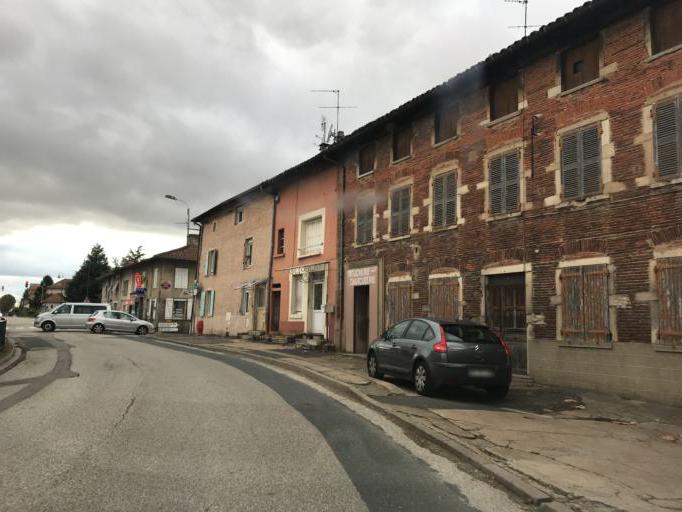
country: FR
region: Rhone-Alpes
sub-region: Departement de l'Ain
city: Villeneuve
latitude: 46.0213
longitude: 4.8367
